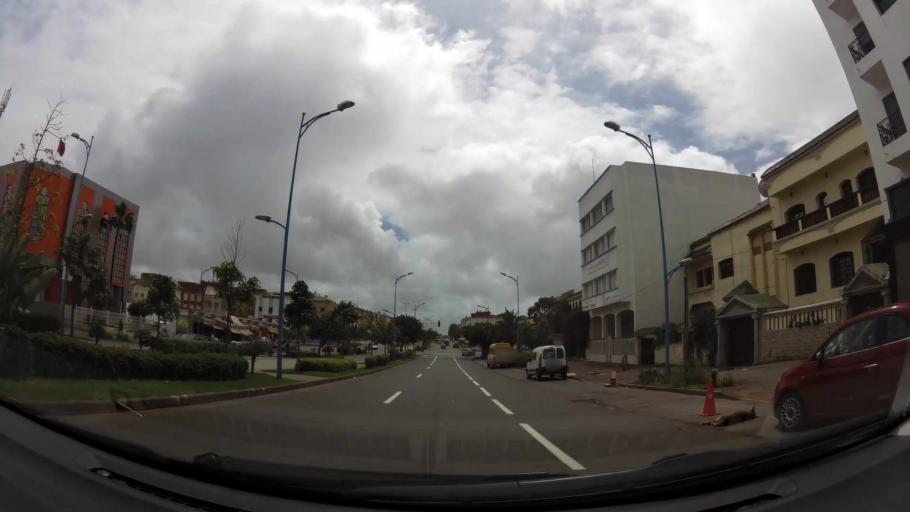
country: MA
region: Grand Casablanca
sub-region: Casablanca
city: Casablanca
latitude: 33.5548
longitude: -7.6812
